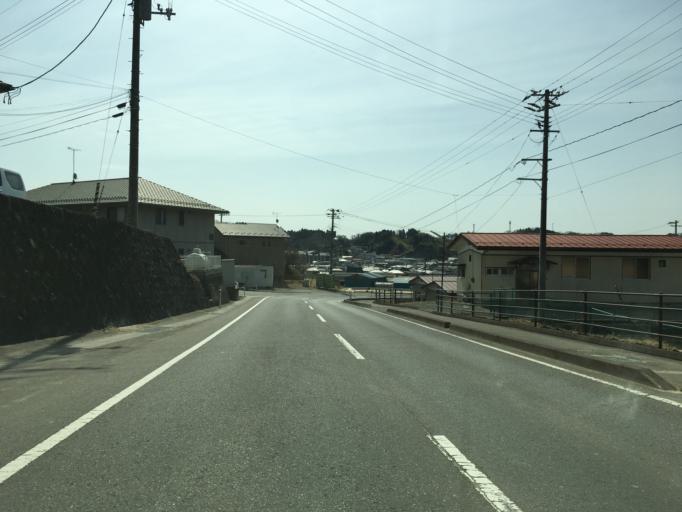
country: JP
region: Fukushima
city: Nihommatsu
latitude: 37.6066
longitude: 140.4467
